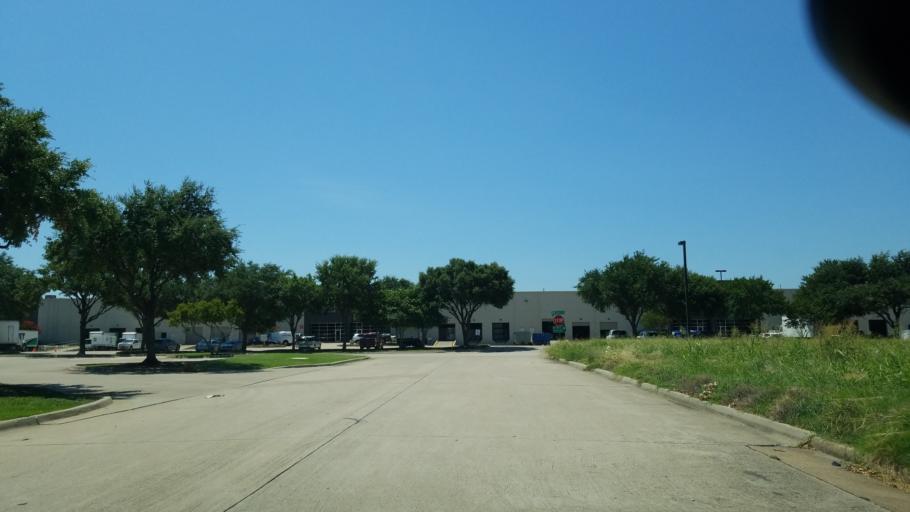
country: US
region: Texas
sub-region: Dallas County
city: Farmers Branch
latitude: 32.9410
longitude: -96.9271
